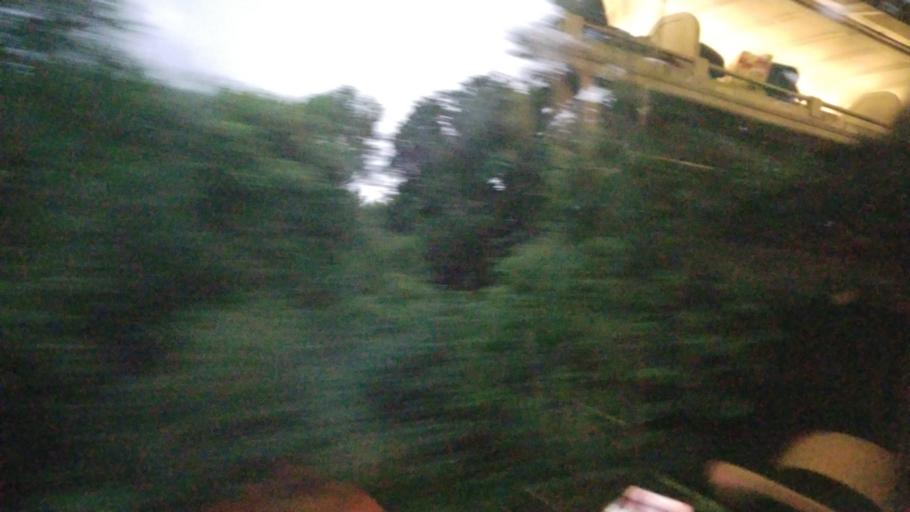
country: US
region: Virginia
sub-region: Orange County
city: Gordonsville
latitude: 38.1808
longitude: -78.2608
